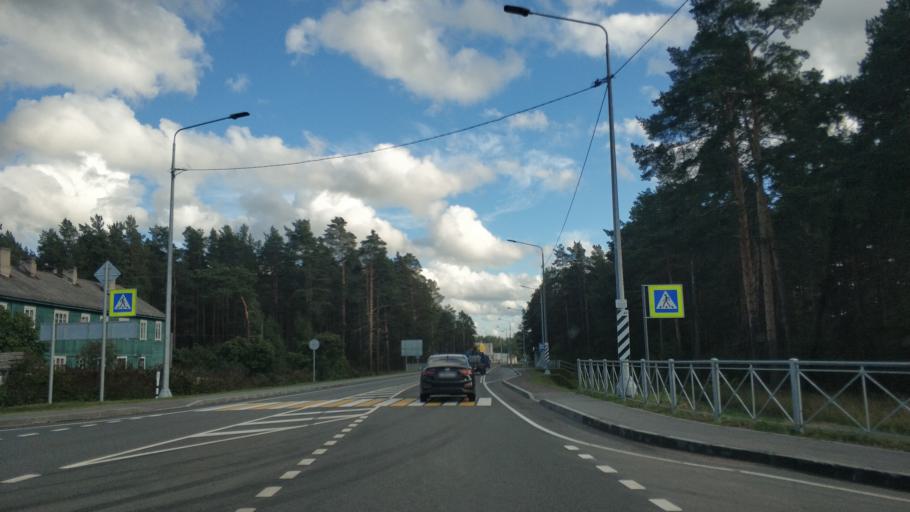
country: RU
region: Leningrad
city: Priozersk
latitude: 61.0053
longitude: 30.1793
